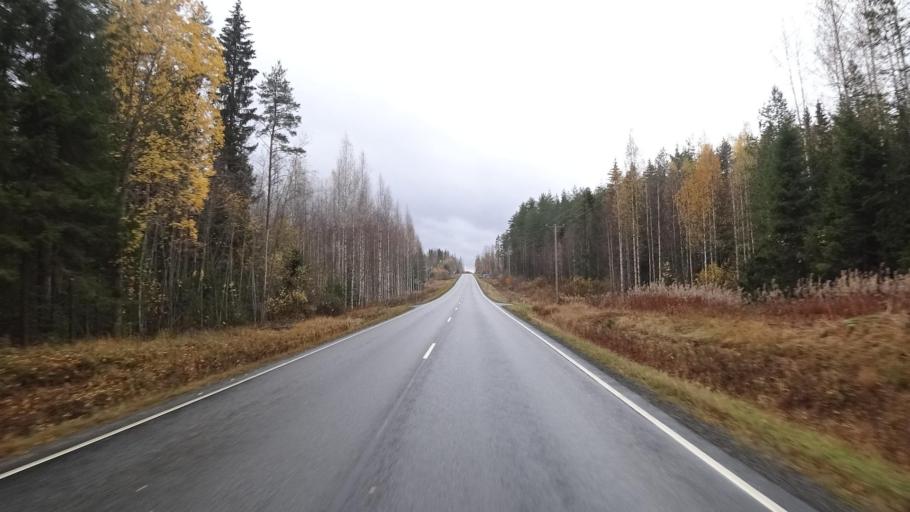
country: FI
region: Southern Savonia
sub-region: Mikkeli
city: Kangasniemi
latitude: 62.1762
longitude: 26.8653
